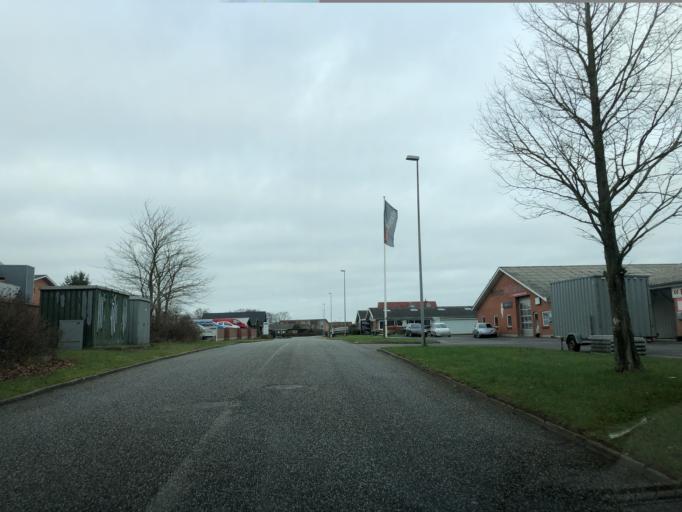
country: DK
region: Central Jutland
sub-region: Viborg Kommune
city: Stoholm
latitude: 56.4778
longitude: 9.1519
